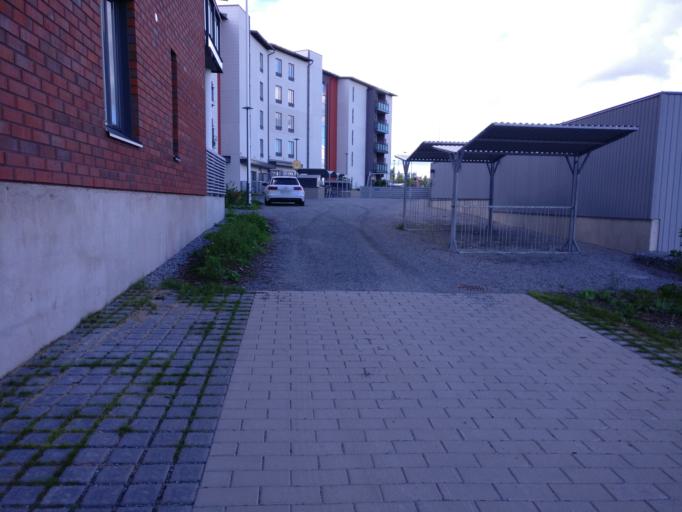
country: FI
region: Pirkanmaa
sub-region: Tampere
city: Tampere
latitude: 61.4337
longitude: 23.8089
